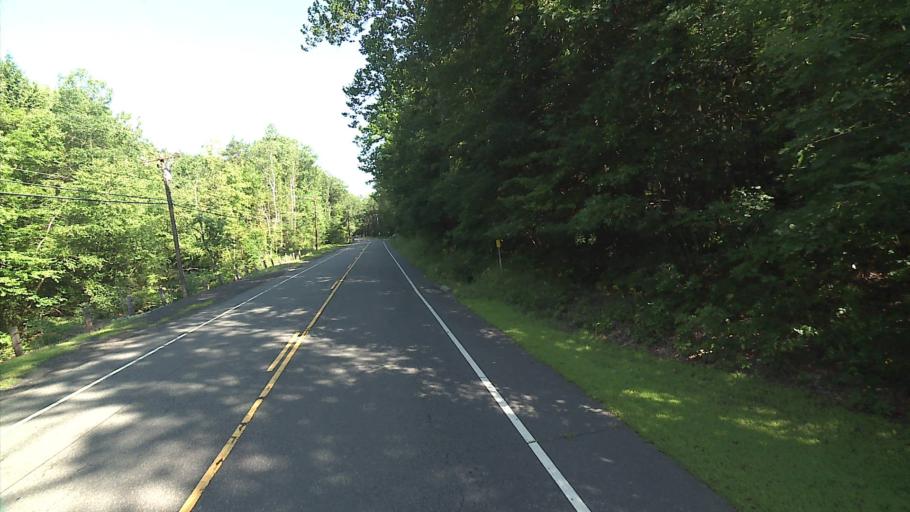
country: US
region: Connecticut
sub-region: Hartford County
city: North Granby
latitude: 41.9660
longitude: -72.8606
